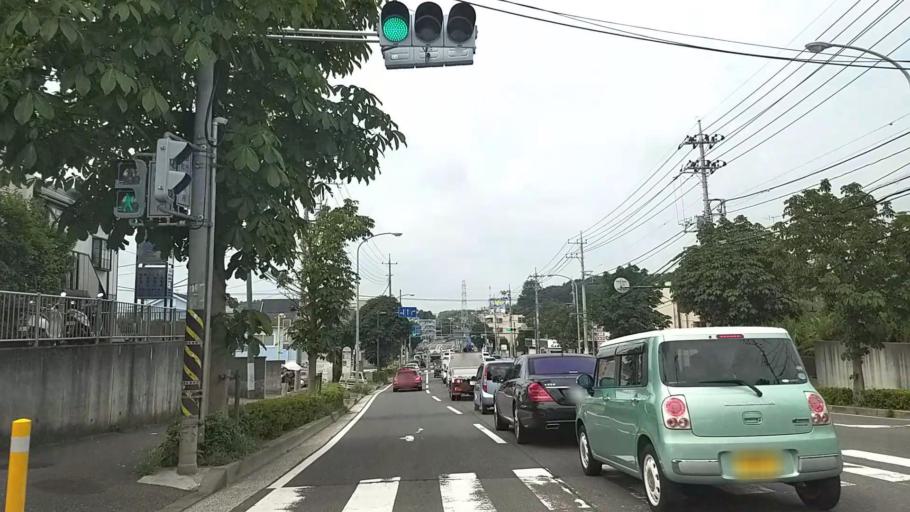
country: JP
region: Kanagawa
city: Minami-rinkan
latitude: 35.4870
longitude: 139.5228
